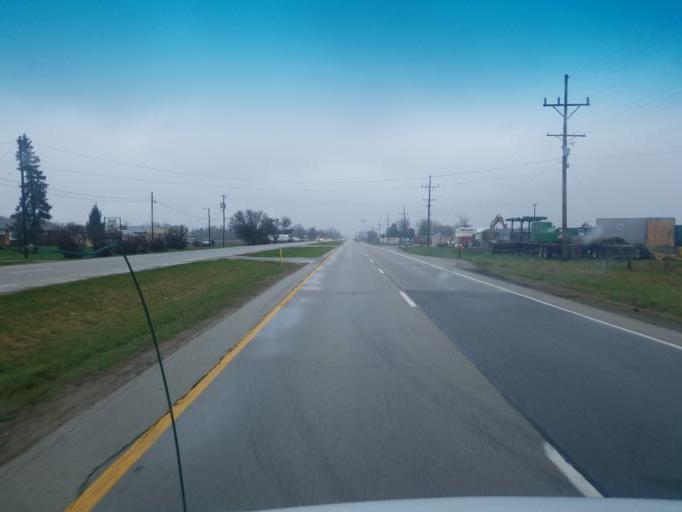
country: US
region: Ohio
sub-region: Wood County
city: Bowling Green
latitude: 41.2797
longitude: -83.6504
